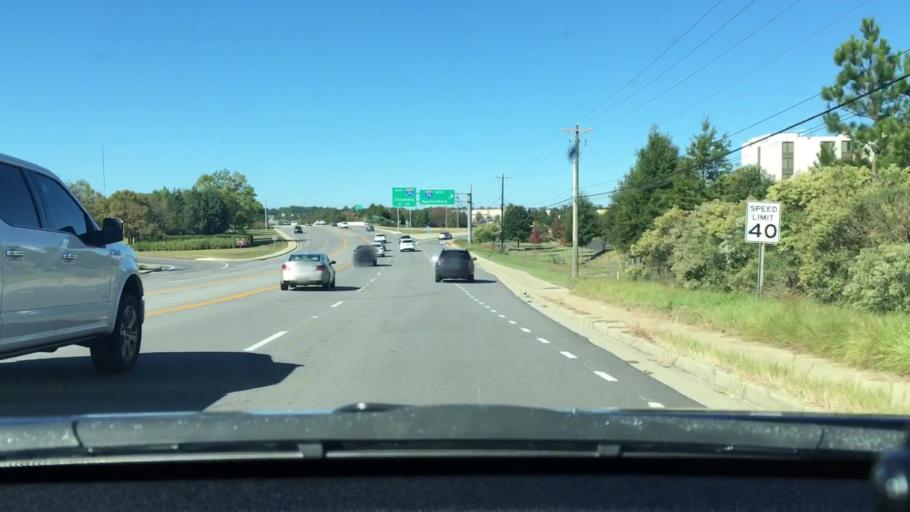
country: US
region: South Carolina
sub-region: Lexington County
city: Irmo
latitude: 34.0904
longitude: -81.1620
